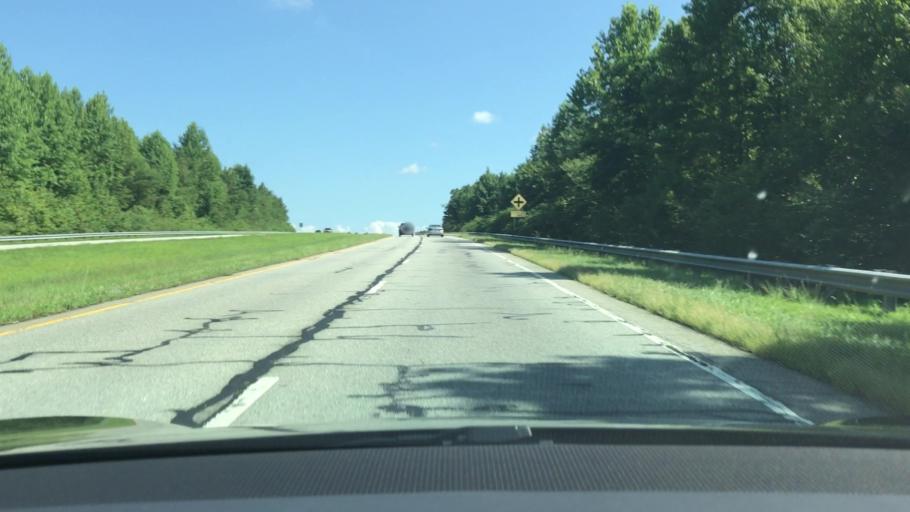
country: US
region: Georgia
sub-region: Habersham County
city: Clarkesville
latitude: 34.6225
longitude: -83.4471
